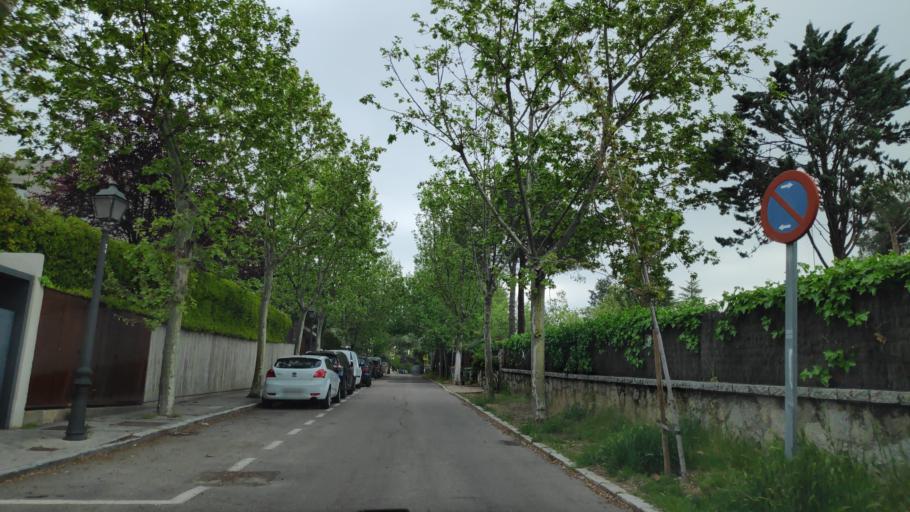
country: ES
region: Madrid
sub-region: Provincia de Madrid
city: Pozuelo de Alarcon
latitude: 40.4626
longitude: -3.7917
